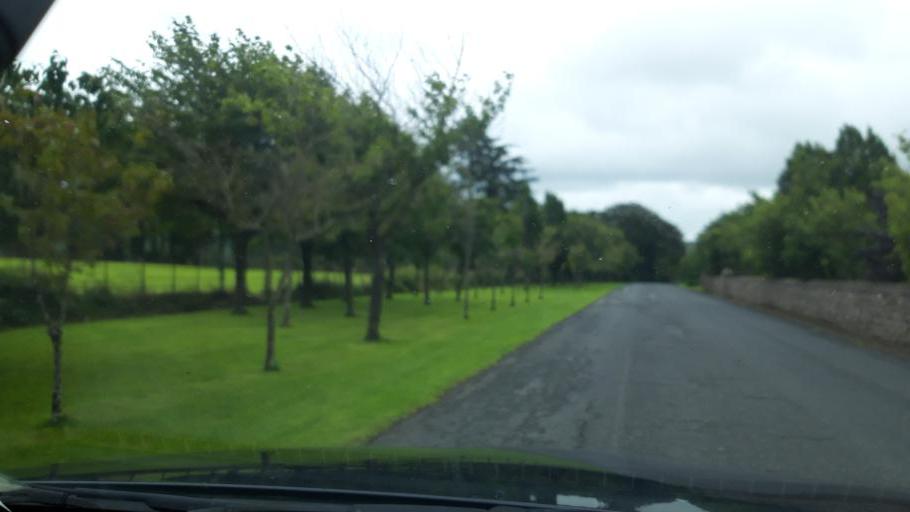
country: IE
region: Munster
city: Cahir
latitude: 52.1856
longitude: -7.8520
